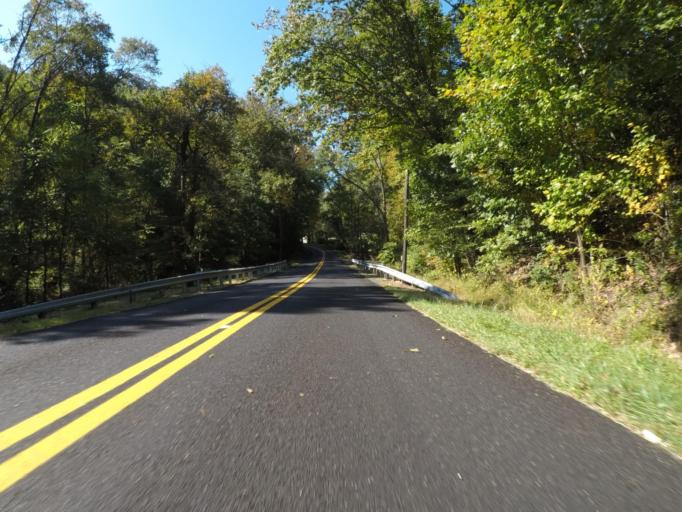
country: US
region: Maryland
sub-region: Carroll County
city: Hampstead
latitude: 39.5876
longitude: -76.9001
